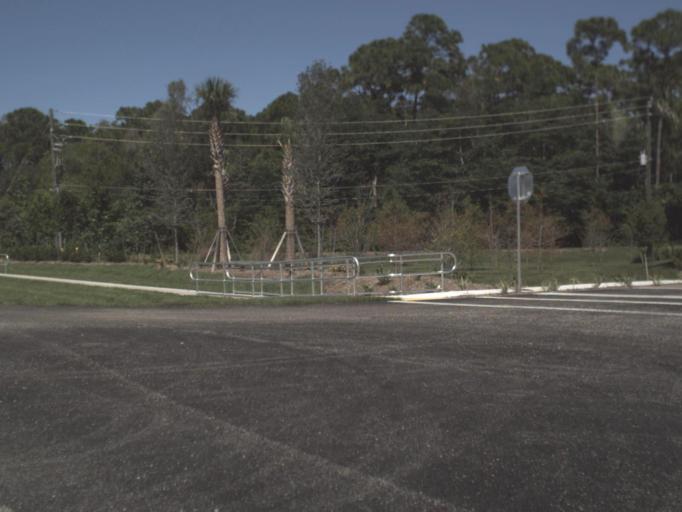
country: US
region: Florida
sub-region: Lee County
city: Estero
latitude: 26.4540
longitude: -81.8224
